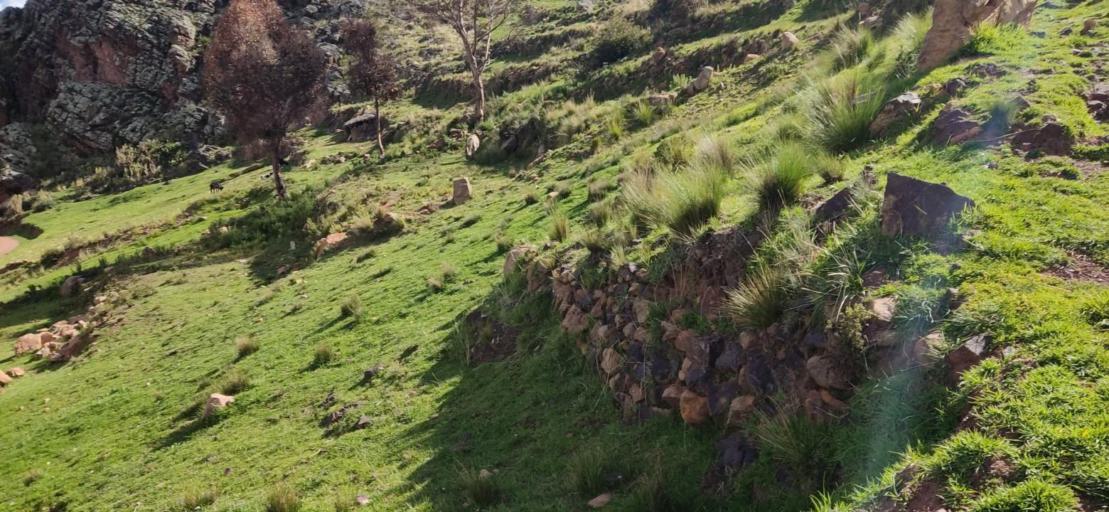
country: BO
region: La Paz
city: Batallas
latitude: -16.3414
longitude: -68.6358
